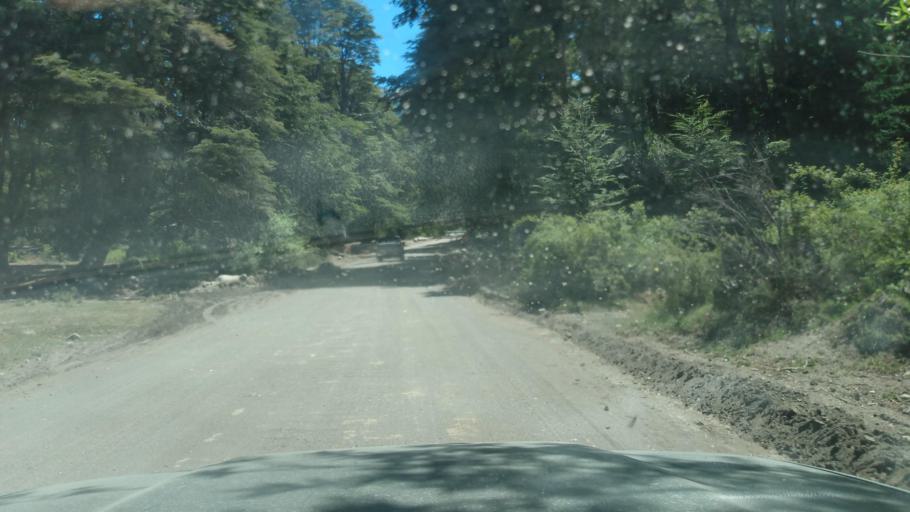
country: AR
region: Neuquen
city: Villa La Angostura
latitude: -40.6285
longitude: -71.4845
